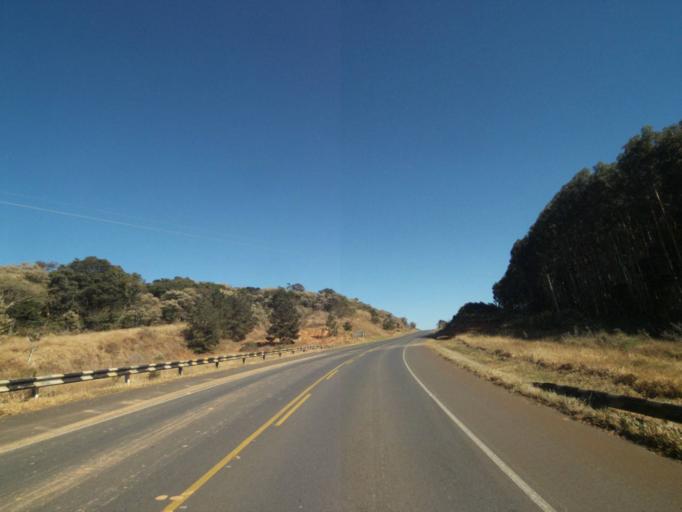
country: BR
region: Parana
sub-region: Tibagi
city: Tibagi
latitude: -24.4073
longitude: -50.3458
